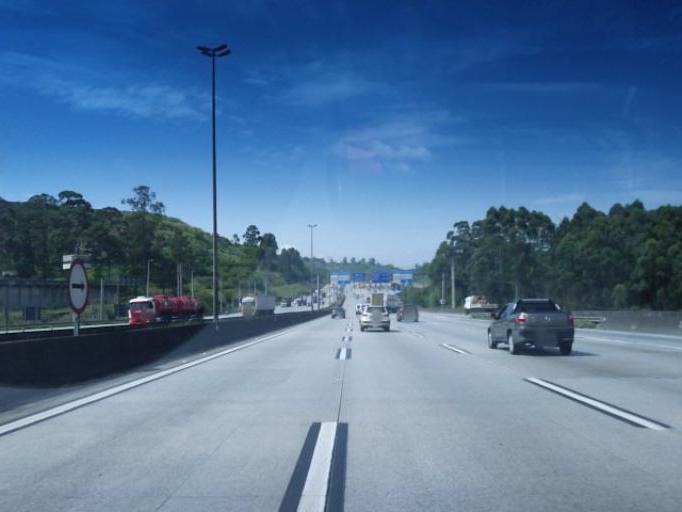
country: BR
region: Sao Paulo
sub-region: Taboao Da Serra
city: Taboao da Serra
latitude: -23.5958
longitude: -46.8113
